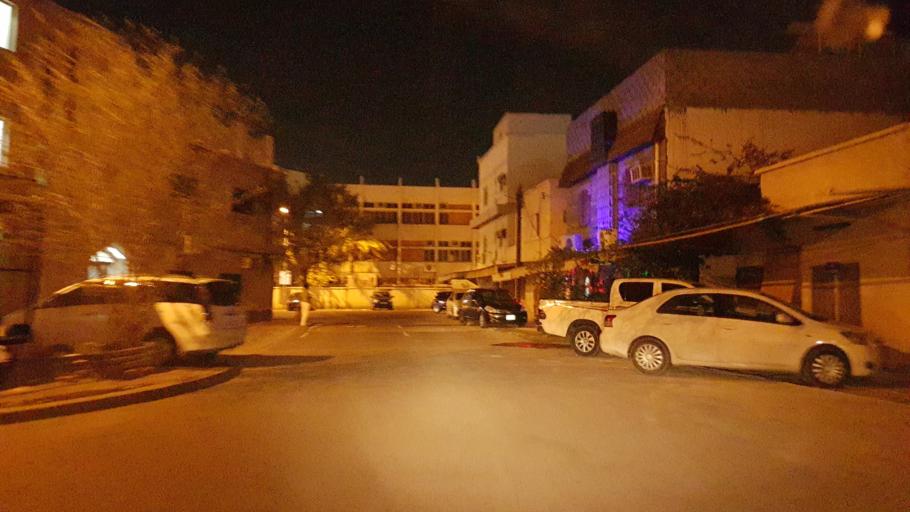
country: BH
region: Muharraq
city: Al Muharraq
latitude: 26.2606
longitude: 50.6169
